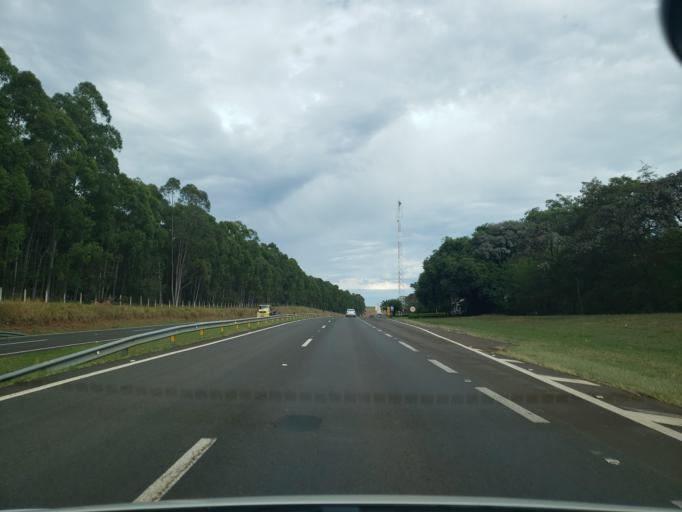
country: BR
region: Sao Paulo
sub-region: Dois Corregos
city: Dois Corregos
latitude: -22.2676
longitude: -48.3888
